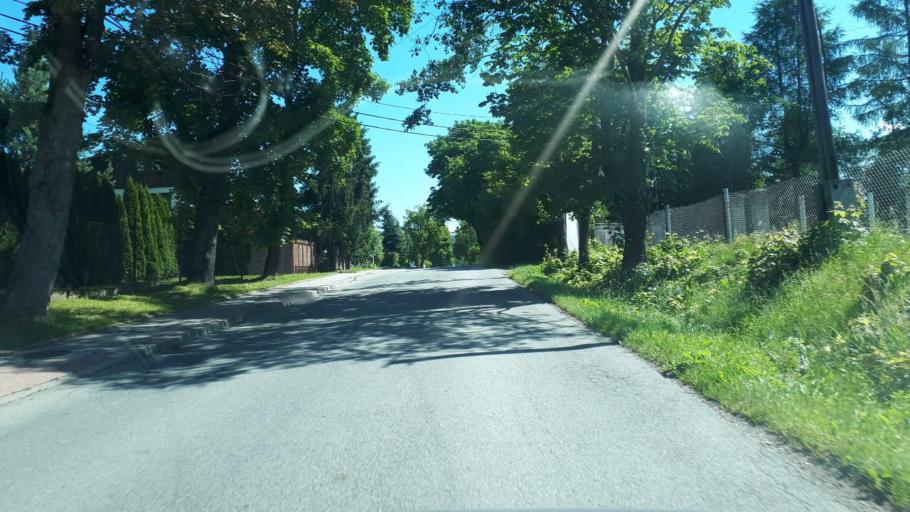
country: PL
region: Silesian Voivodeship
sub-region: Powiat zywiecki
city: Lodygowice
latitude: 49.7183
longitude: 19.1442
